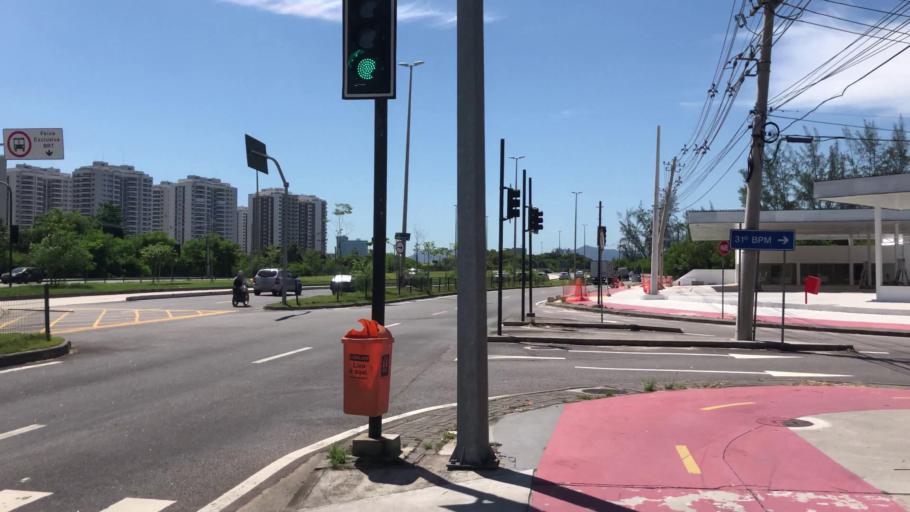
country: BR
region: Rio de Janeiro
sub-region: Nilopolis
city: Nilopolis
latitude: -22.9736
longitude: -43.3966
